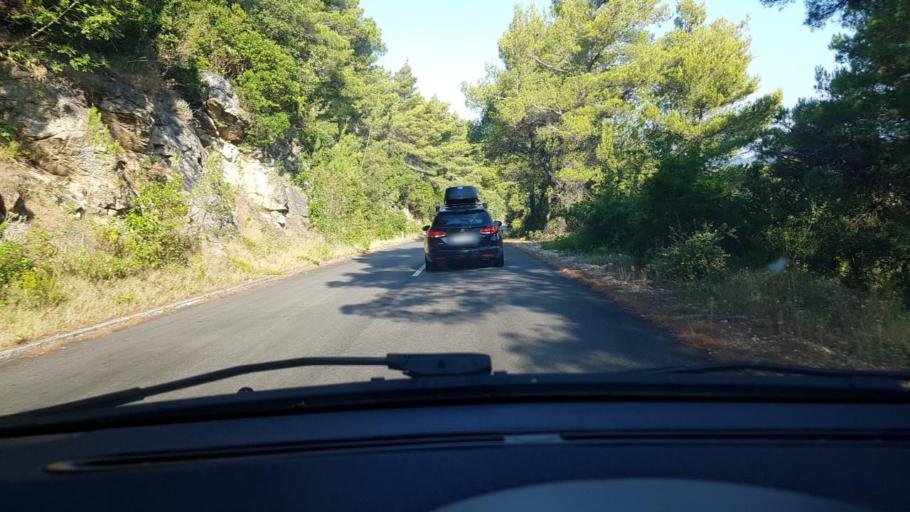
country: HR
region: Dubrovacko-Neretvanska
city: Blato
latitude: 42.7527
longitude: 17.4913
